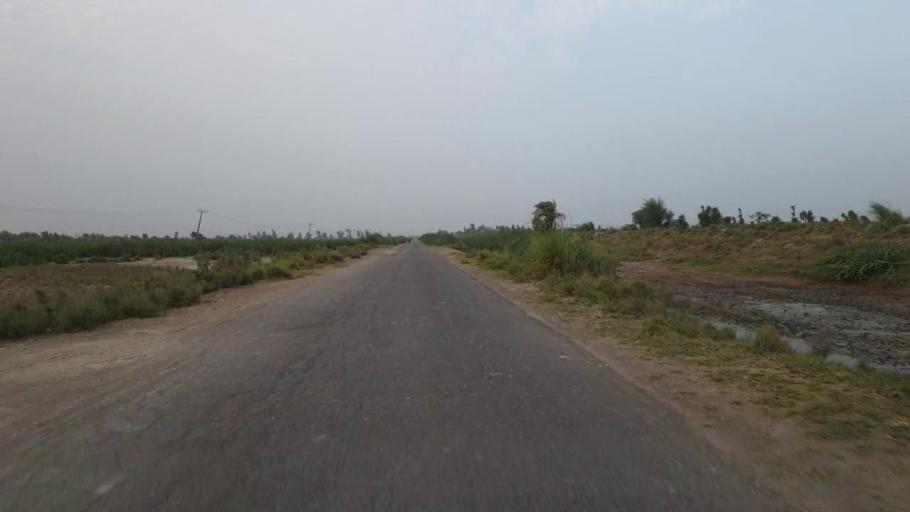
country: PK
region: Sindh
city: Daur
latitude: 26.4511
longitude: 68.2889
